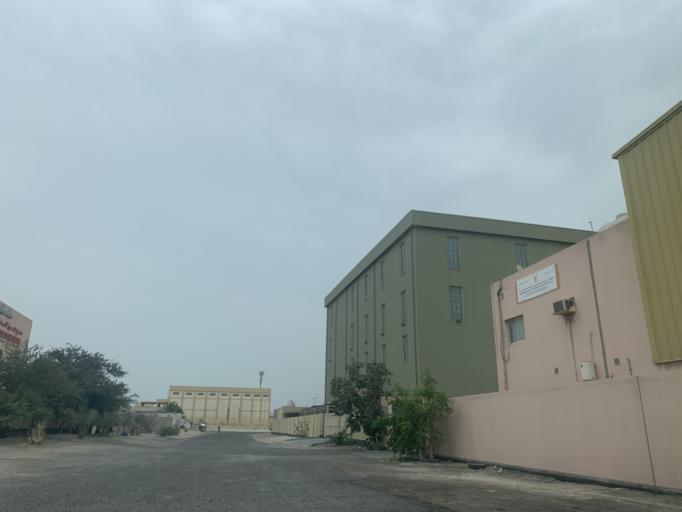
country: BH
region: Muharraq
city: Al Hadd
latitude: 26.2127
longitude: 50.6643
